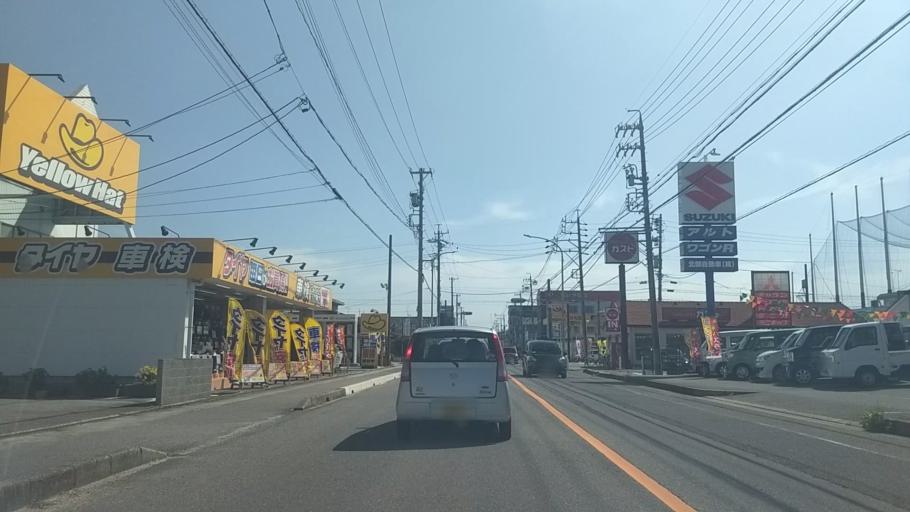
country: JP
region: Aichi
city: Okazaki
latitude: 34.9758
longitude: 137.1358
